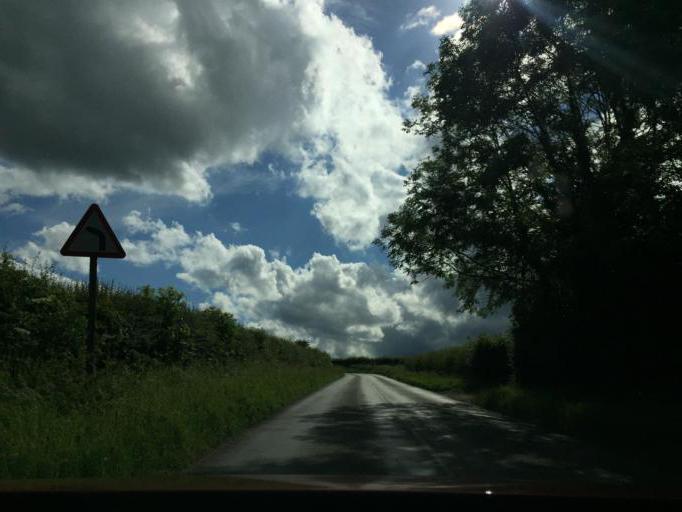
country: GB
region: England
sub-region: Hertfordshire
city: Harpenden
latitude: 51.8474
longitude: -0.3823
